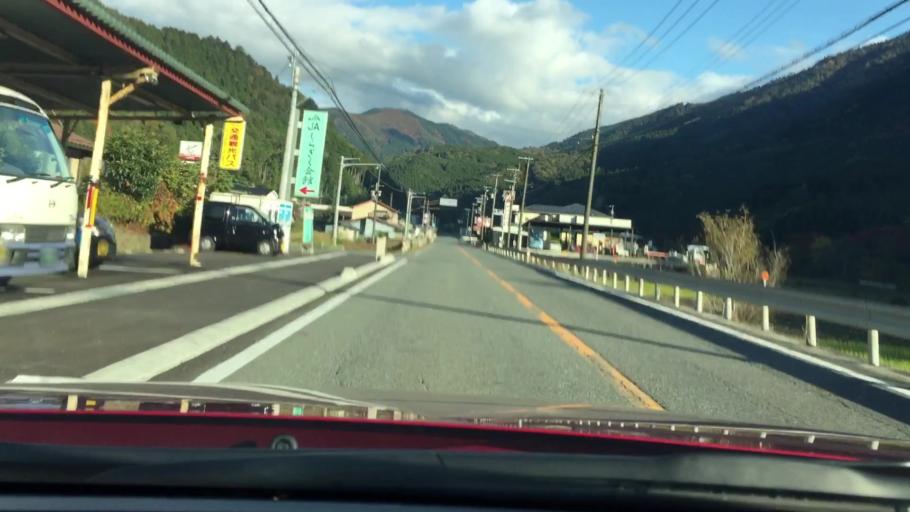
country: JP
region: Hyogo
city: Yamazakicho-nakabirose
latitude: 35.1219
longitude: 134.5690
